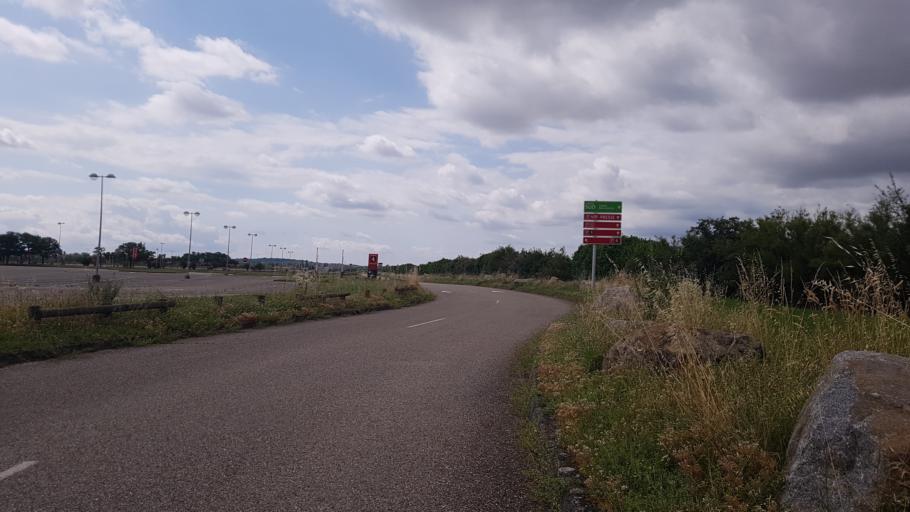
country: FR
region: Rhone-Alpes
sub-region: Departement du Rhone
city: Bron
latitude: 45.7304
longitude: 4.9457
